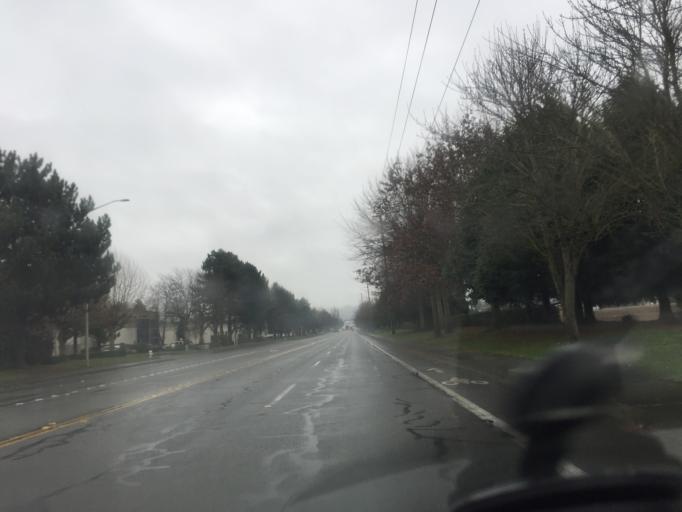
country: US
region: Washington
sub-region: King County
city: SeaTac
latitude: 47.4267
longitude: -122.2567
